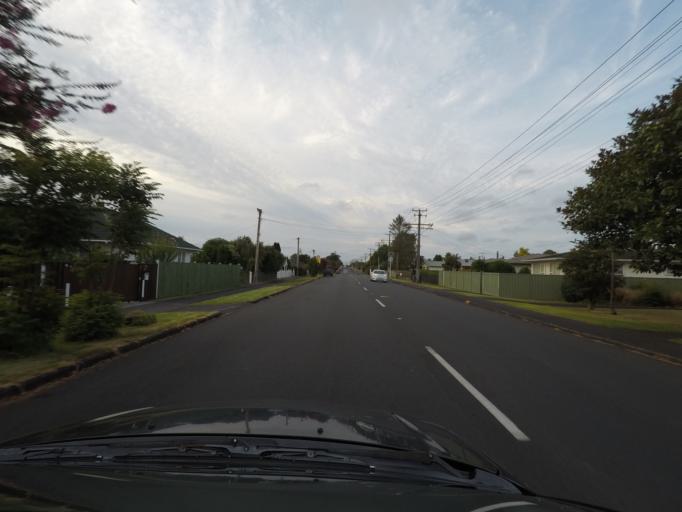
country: NZ
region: Auckland
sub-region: Auckland
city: Rosebank
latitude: -36.8385
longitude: 174.6510
